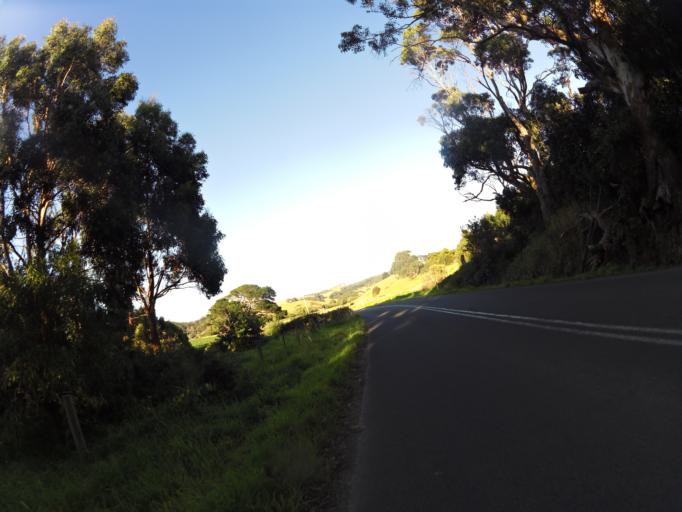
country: AU
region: Victoria
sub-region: Colac-Otway
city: Apollo Bay
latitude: -38.7675
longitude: 143.6534
